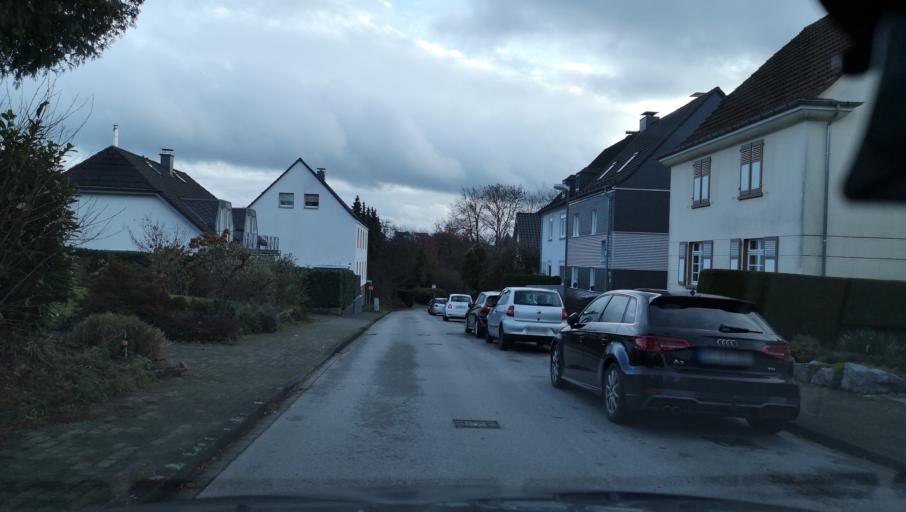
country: DE
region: North Rhine-Westphalia
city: Radevormwald
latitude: 51.1999
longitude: 7.3665
